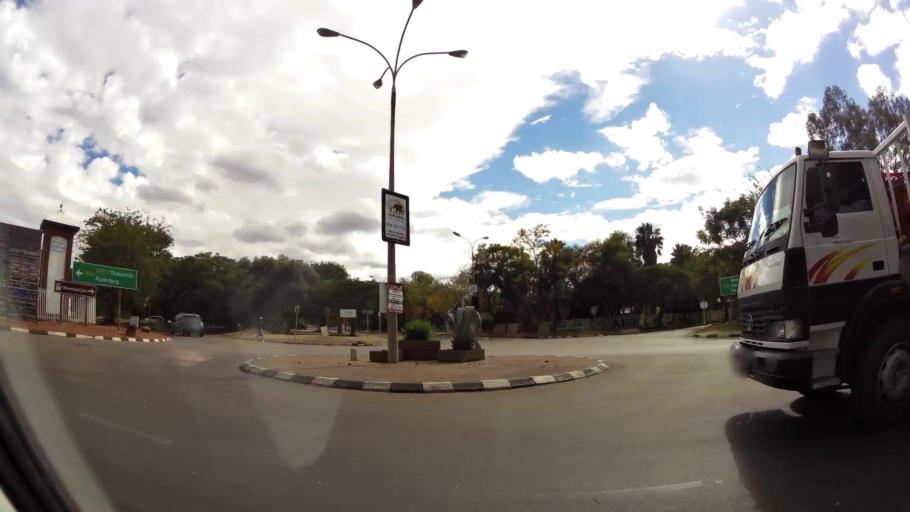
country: ZA
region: Limpopo
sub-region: Waterberg District Municipality
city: Warmbaths
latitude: -24.8857
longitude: 28.2846
